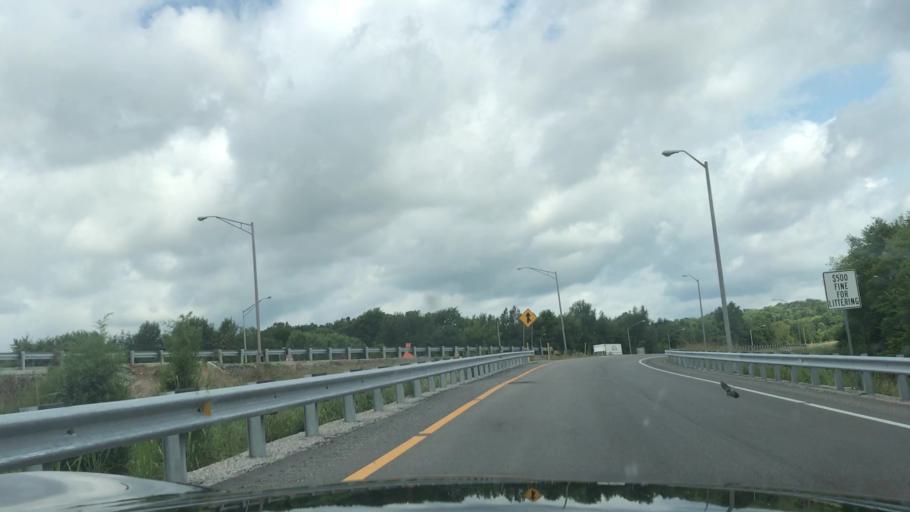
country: US
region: Kentucky
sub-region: Warren County
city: Bowling Green
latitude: 36.9587
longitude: -86.4968
